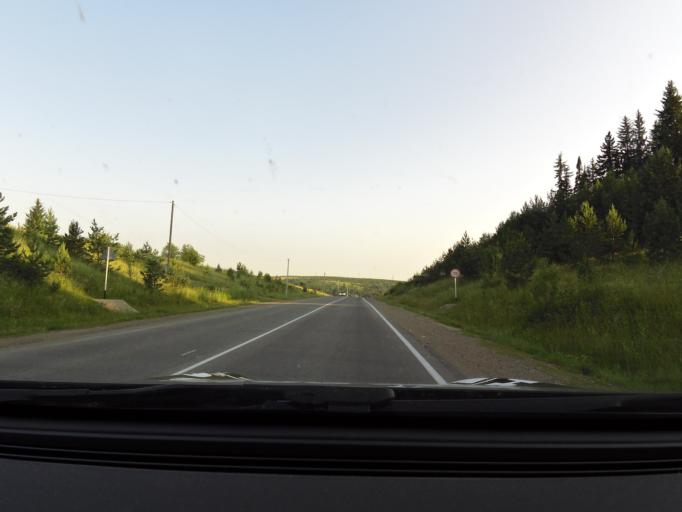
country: RU
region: Sverdlovsk
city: Mikhaylovsk
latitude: 56.4653
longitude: 59.1055
